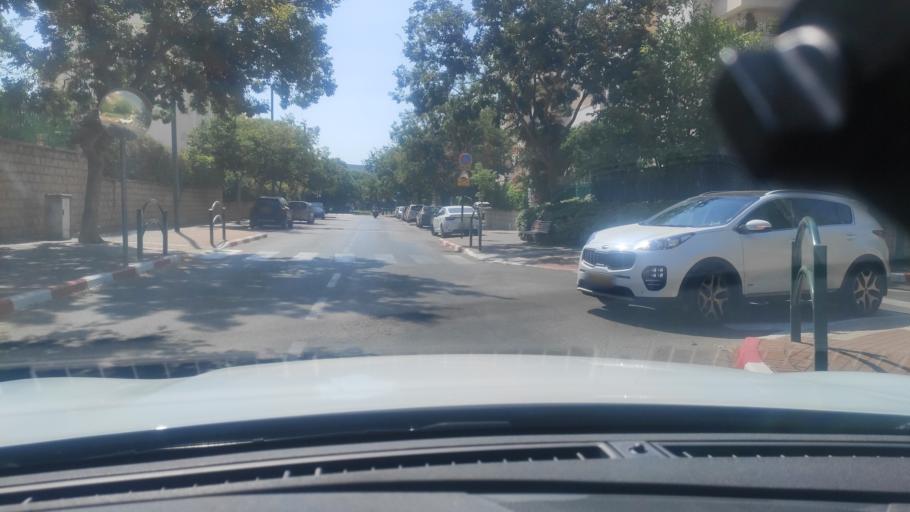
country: IL
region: Central District
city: Kfar Saba
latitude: 32.1790
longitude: 34.9339
